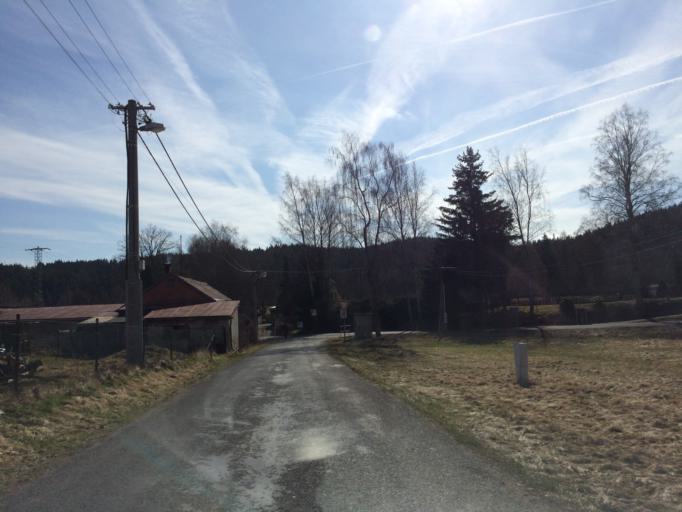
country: CZ
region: Karlovarsky
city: Nejdek
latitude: 50.3185
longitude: 12.7013
